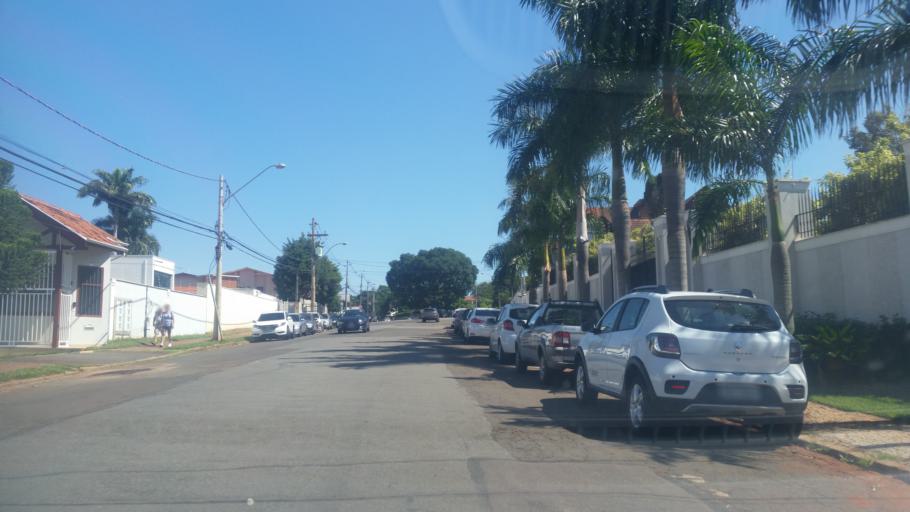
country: BR
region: Sao Paulo
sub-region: Campinas
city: Campinas
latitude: -22.8707
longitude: -47.0576
